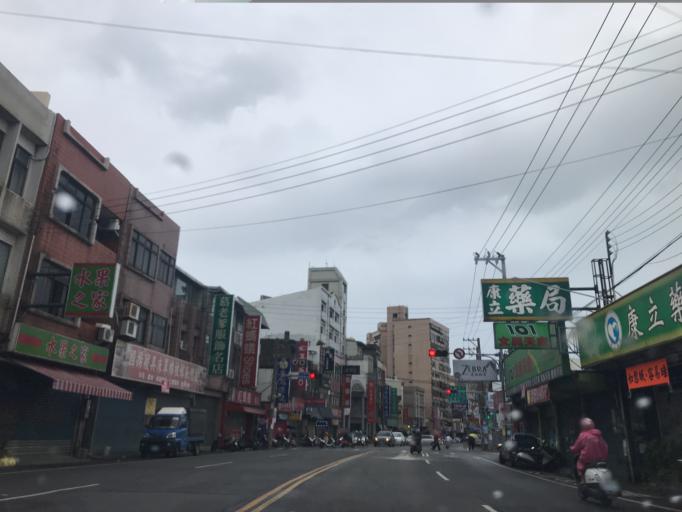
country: TW
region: Taiwan
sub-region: Hsinchu
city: Zhubei
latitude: 24.8352
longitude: 121.0125
